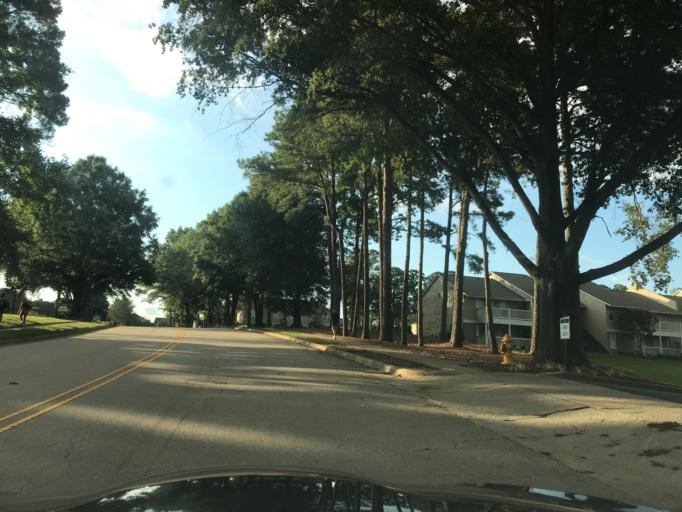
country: US
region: North Carolina
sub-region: Wake County
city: West Raleigh
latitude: 35.8666
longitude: -78.6318
